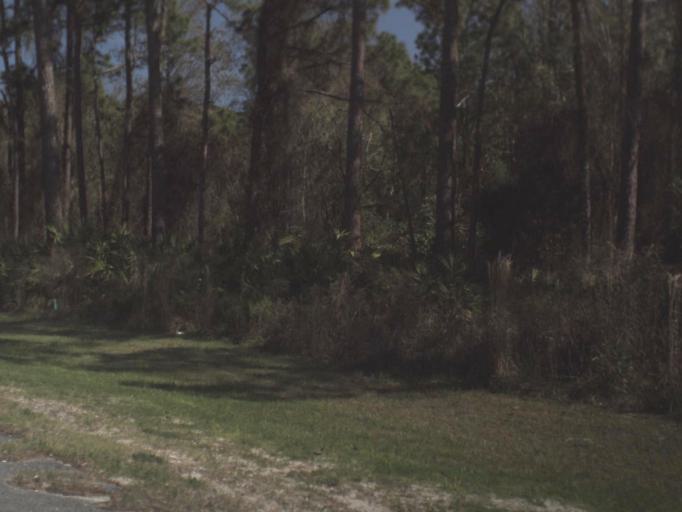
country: US
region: Florida
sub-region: Franklin County
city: Eastpoint
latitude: 29.7361
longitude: -84.8904
